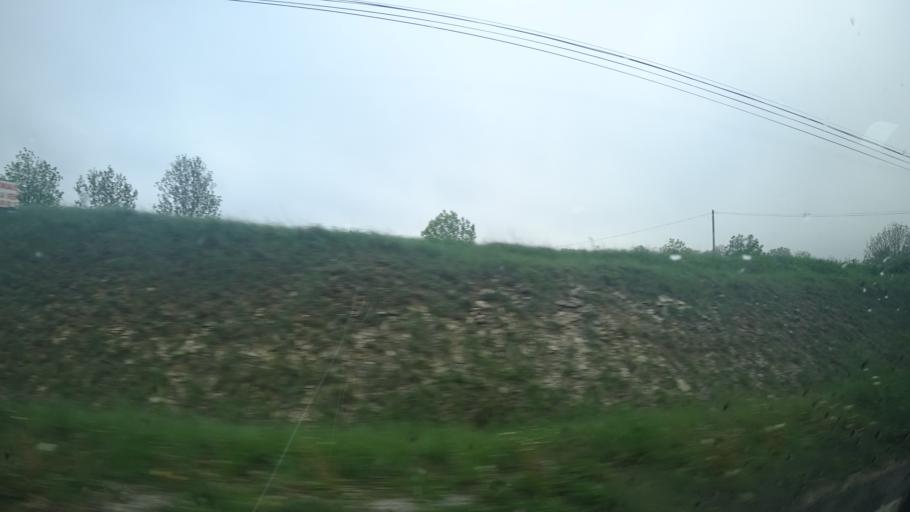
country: FR
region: Midi-Pyrenees
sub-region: Departement de l'Aveyron
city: Severac-le-Chateau
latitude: 44.2106
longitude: 3.0140
